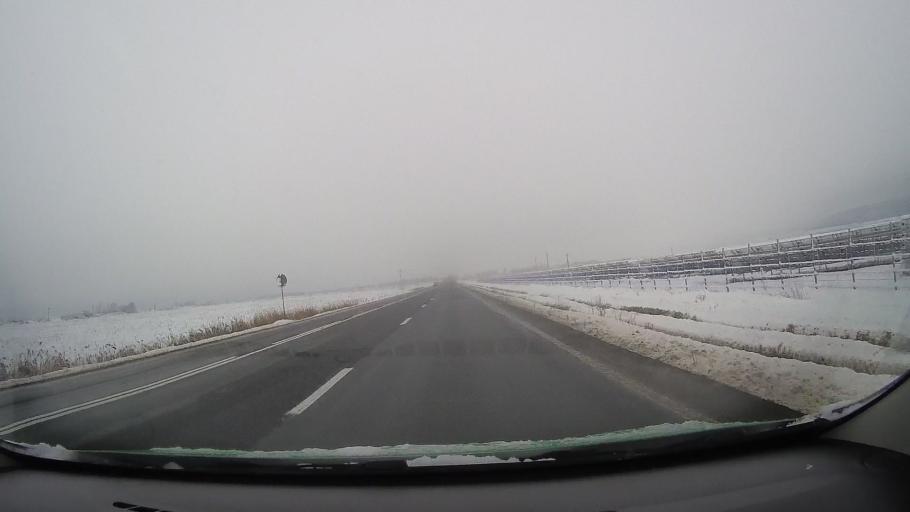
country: RO
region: Sibiu
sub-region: Oras Saliste
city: Saliste
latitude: 45.7911
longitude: 23.9219
